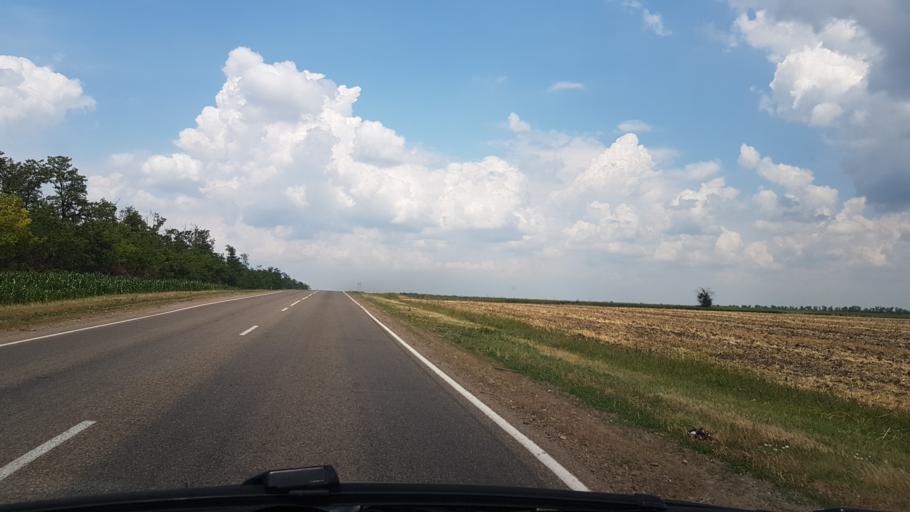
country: RU
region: Krasnodarskiy
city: Dmitriyevskaya
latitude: 45.6782
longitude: 40.7440
